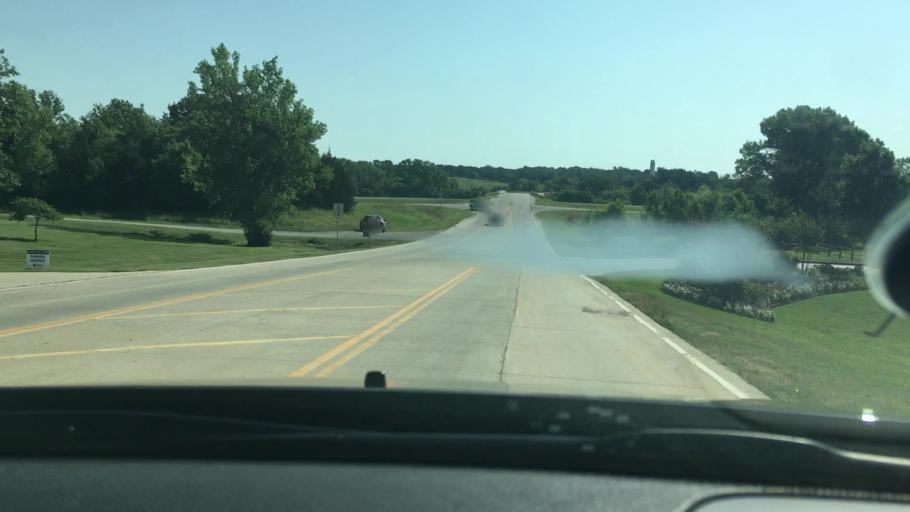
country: US
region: Oklahoma
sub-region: Pontotoc County
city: Ada
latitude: 34.7368
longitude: -96.6477
